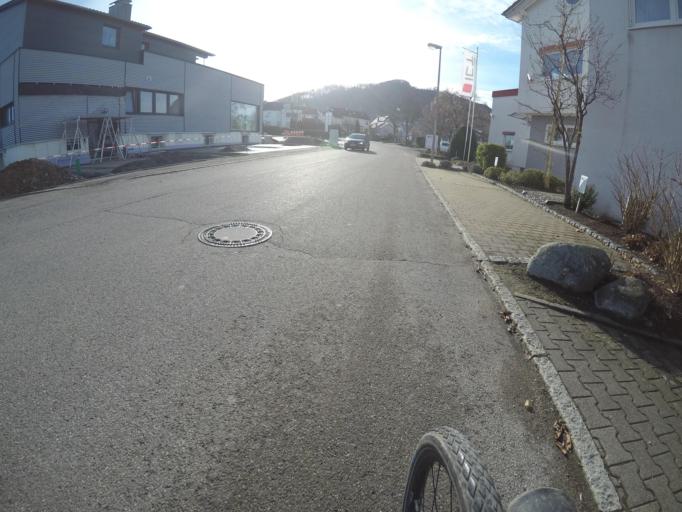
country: DE
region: Baden-Wuerttemberg
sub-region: Regierungsbezirk Stuttgart
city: Kohlberg
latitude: 48.5604
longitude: 9.3425
